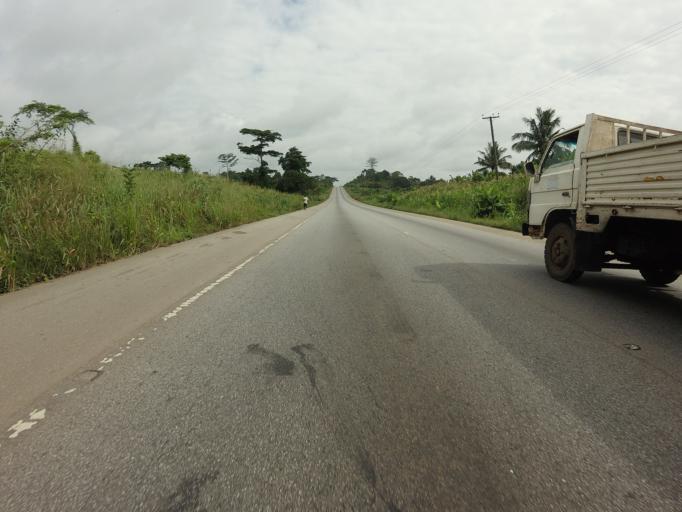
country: GH
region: Ashanti
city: Tafo
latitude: 6.9870
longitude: -1.6900
